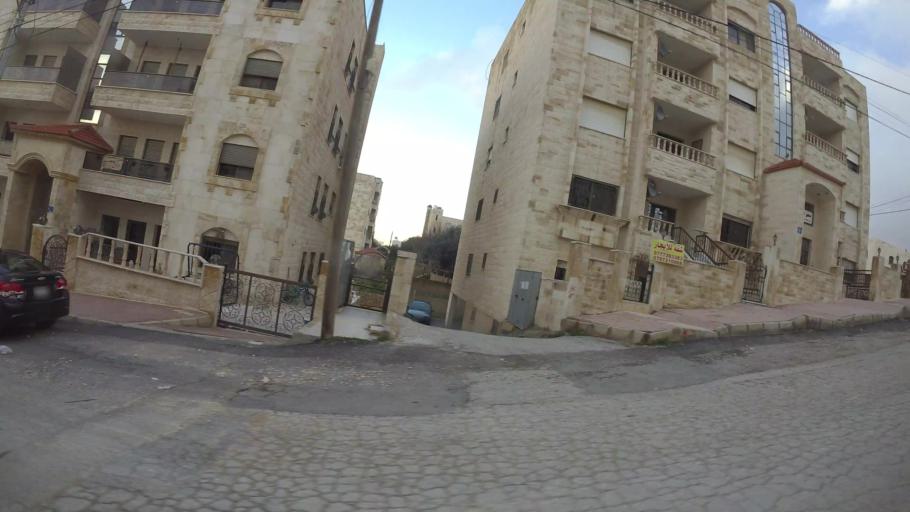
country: JO
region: Amman
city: Al Jubayhah
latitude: 32.0496
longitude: 35.8952
